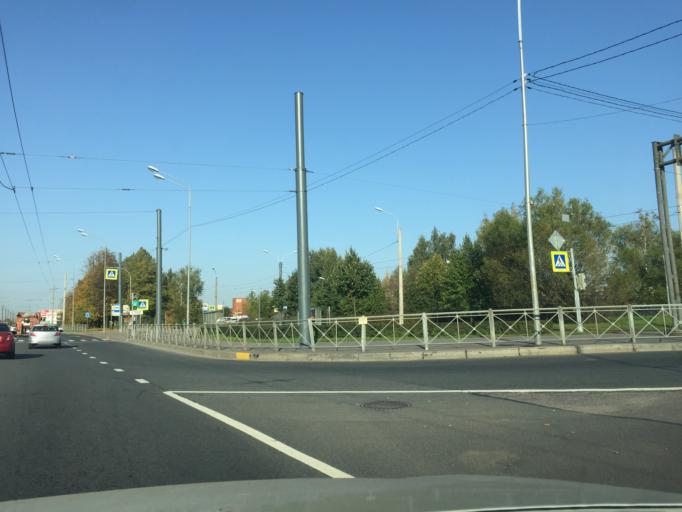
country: RU
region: St.-Petersburg
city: Krasnogvargeisky
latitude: 59.9971
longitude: 30.4380
